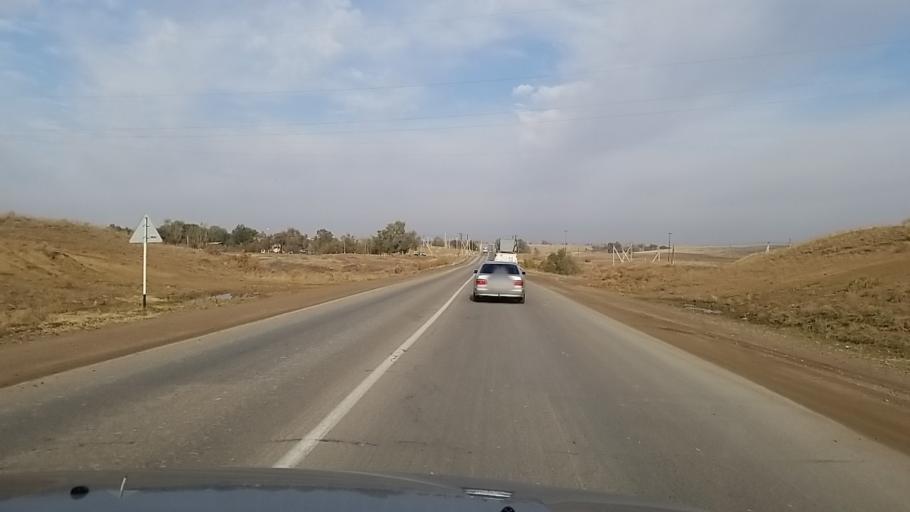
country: KZ
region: Almaty Oblysy
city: Burunday
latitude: 43.4660
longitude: 76.7051
